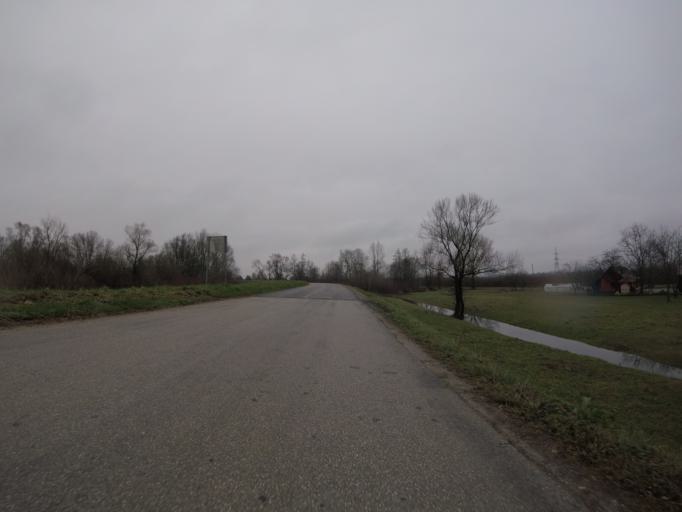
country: HR
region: Sisacko-Moslavacka
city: Lekenik
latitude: 45.6691
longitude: 16.2445
